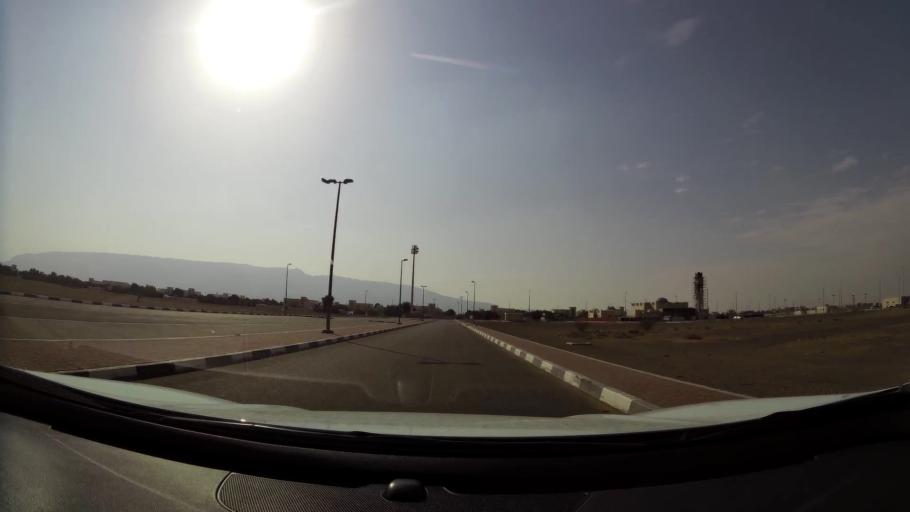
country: AE
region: Abu Dhabi
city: Al Ain
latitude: 24.0890
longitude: 55.8677
